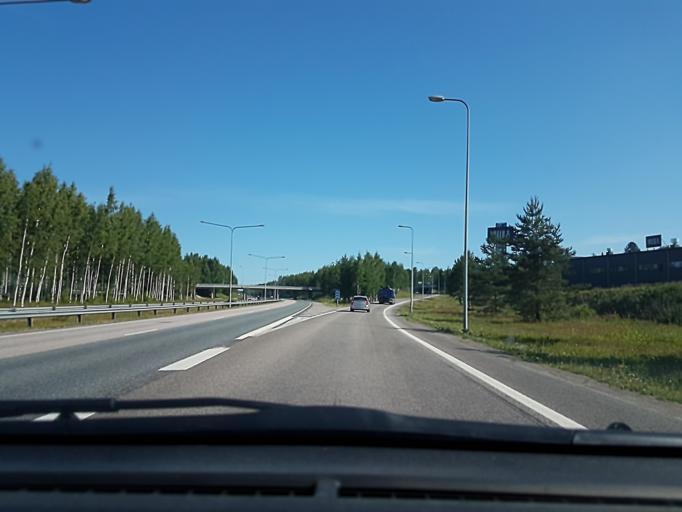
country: FI
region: Uusimaa
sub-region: Helsinki
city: Vantaa
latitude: 60.3386
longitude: 25.0011
